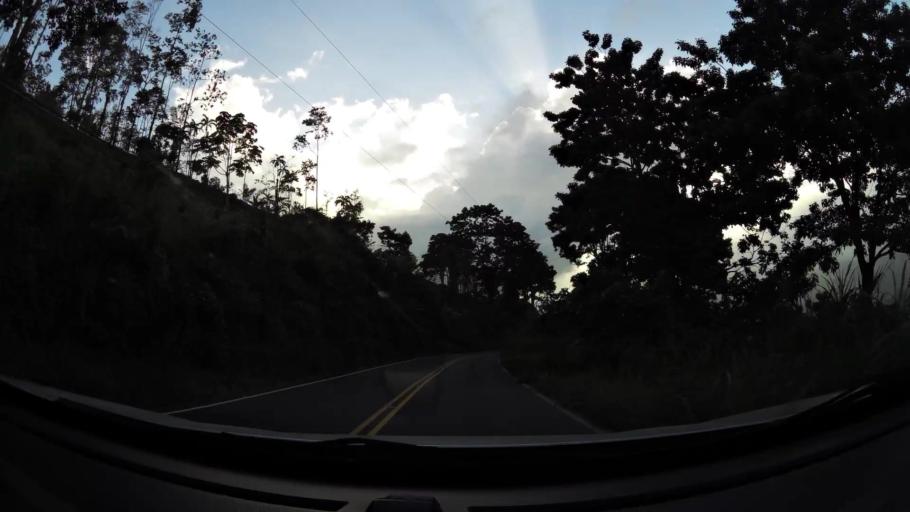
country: CR
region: Limon
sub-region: Canton de Siquirres
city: Siquirres
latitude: 10.0063
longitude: -83.5697
